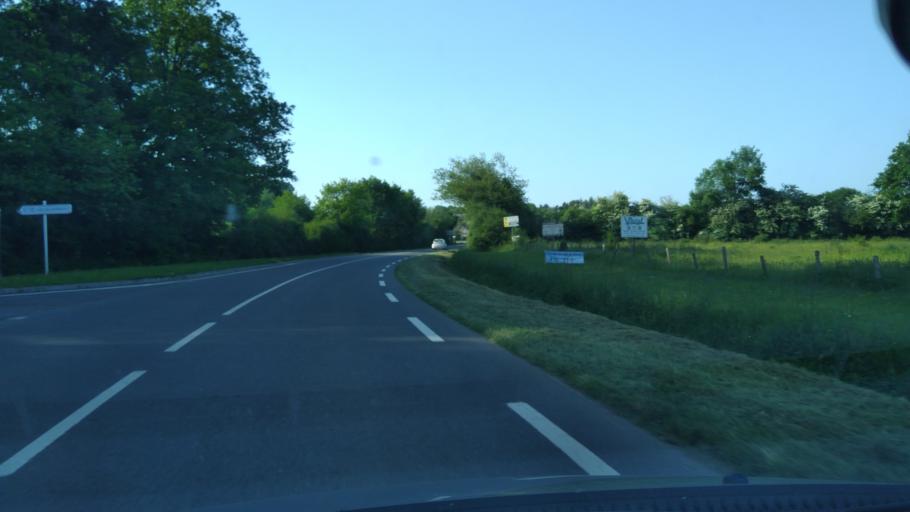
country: FR
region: Pays de la Loire
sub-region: Departement de la Loire-Atlantique
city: La Meilleraye-de-Bretagne
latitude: 47.5503
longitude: -1.4054
